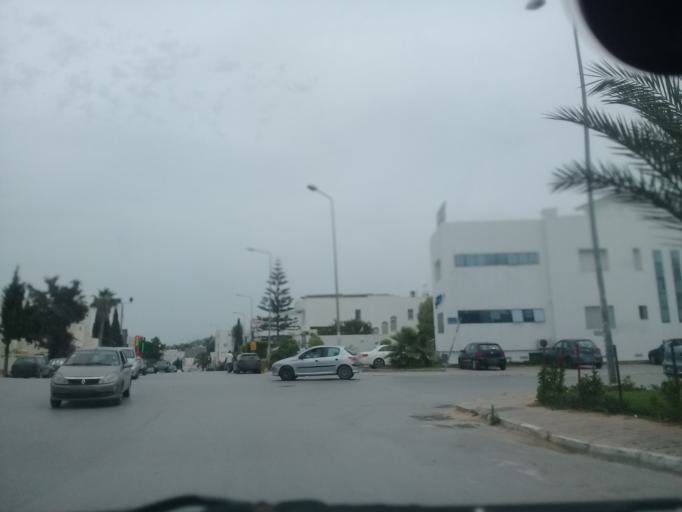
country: TN
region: Tunis
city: Tunis
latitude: 36.8428
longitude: 10.1591
